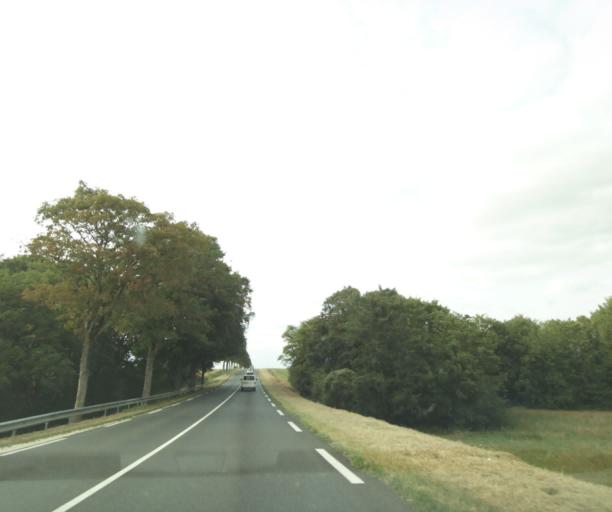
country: FR
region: Centre
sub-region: Departement d'Indre-et-Loire
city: Reignac-sur-Indre
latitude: 47.2307
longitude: 0.8753
